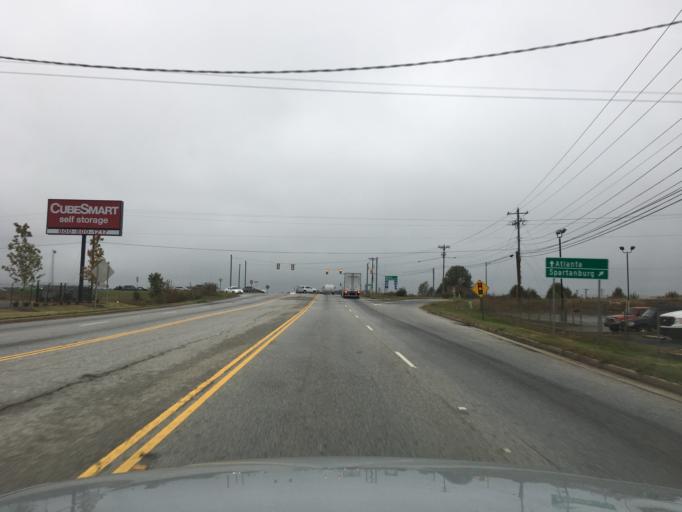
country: US
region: South Carolina
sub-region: Greenville County
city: Five Forks
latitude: 34.8579
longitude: -82.2575
